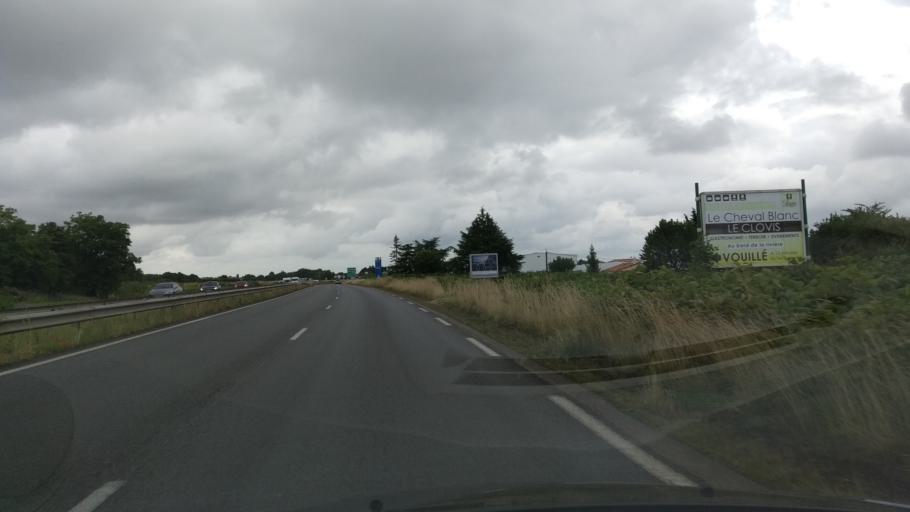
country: FR
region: Poitou-Charentes
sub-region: Departement de la Vienne
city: Poitiers
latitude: 46.5955
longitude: 0.3185
